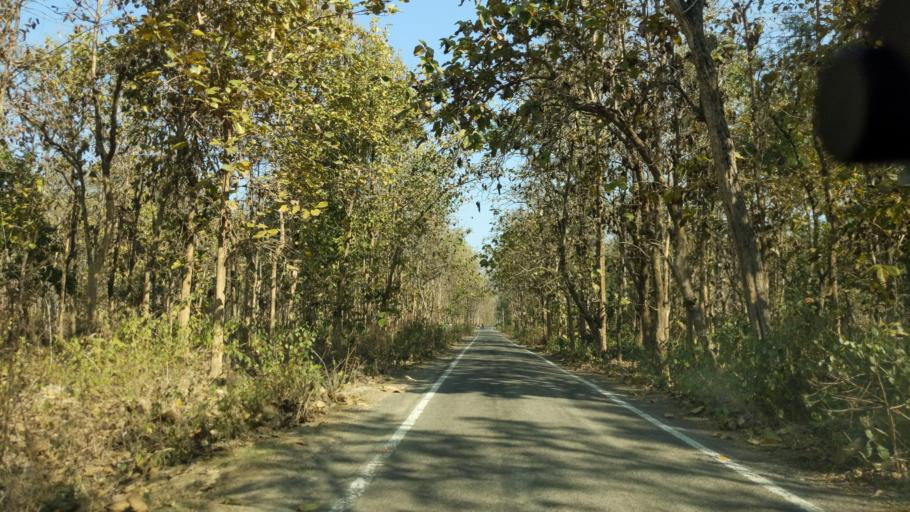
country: IN
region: Uttarakhand
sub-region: Naini Tal
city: Ramnagar
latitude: 29.4253
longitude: 79.1395
